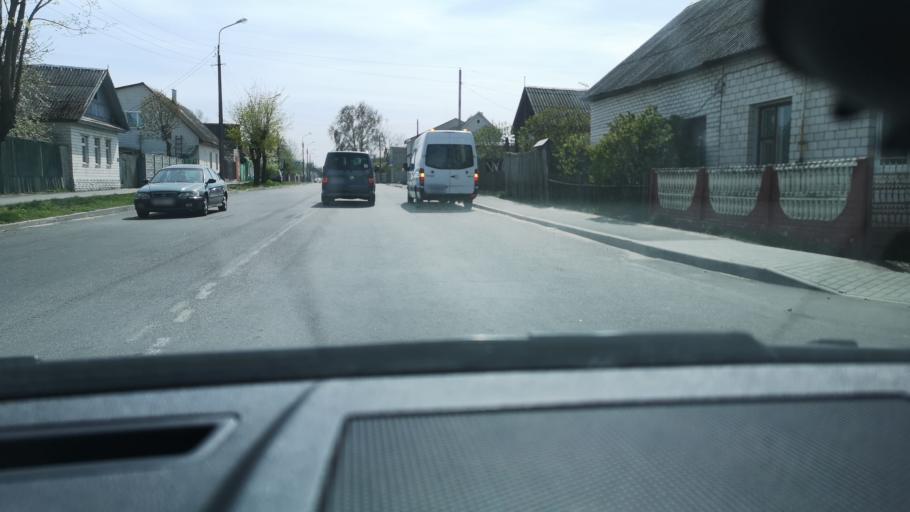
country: BY
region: Gomel
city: Gomel
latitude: 52.4165
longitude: 30.9851
